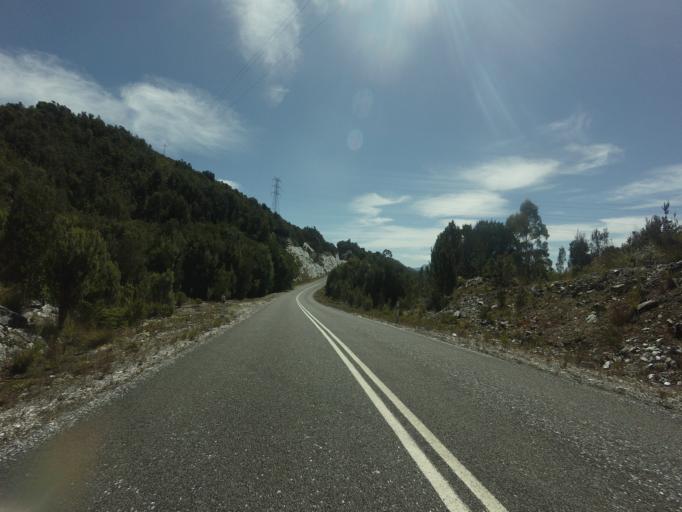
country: AU
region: Tasmania
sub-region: West Coast
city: Queenstown
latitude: -42.7571
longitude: 146.0027
